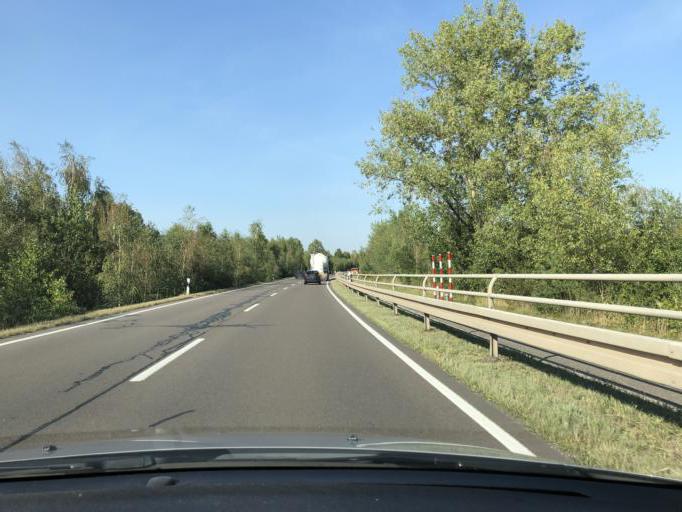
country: DE
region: Saxony-Anhalt
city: Frankleben
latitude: 51.3003
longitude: 11.9188
